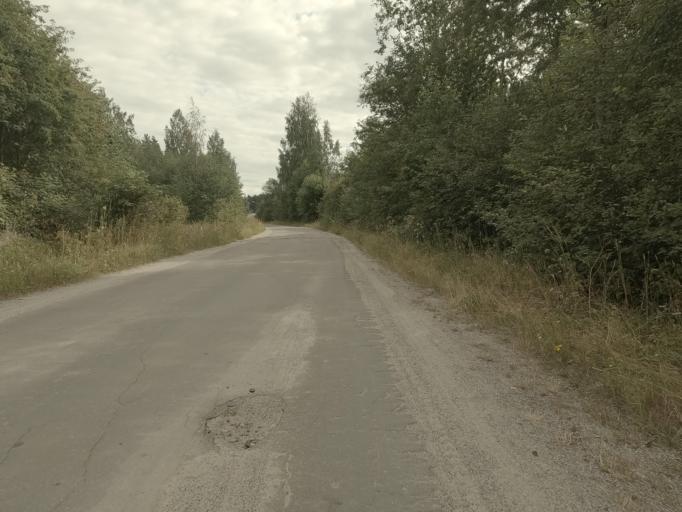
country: RU
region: Leningrad
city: Kamennogorsk
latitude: 60.9685
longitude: 29.1381
